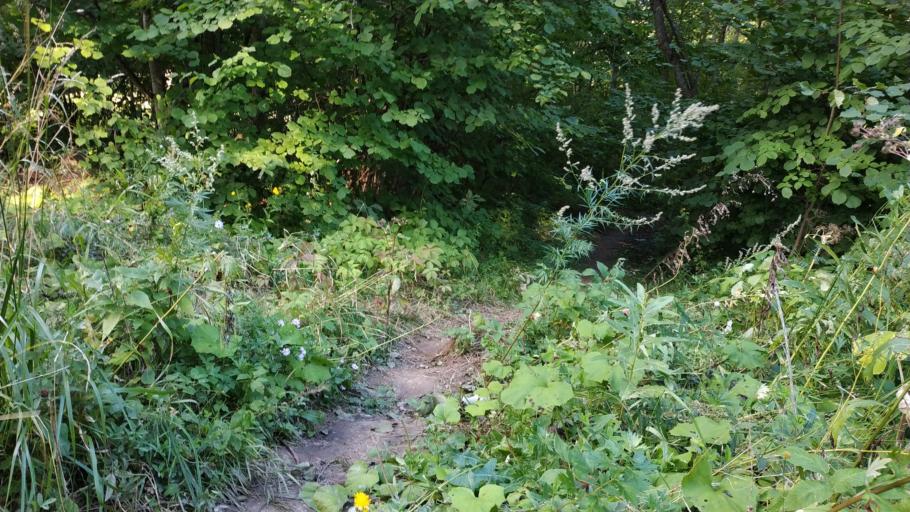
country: RU
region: Chuvashia
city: Novyye Lapsary
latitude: 56.1245
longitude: 47.1229
